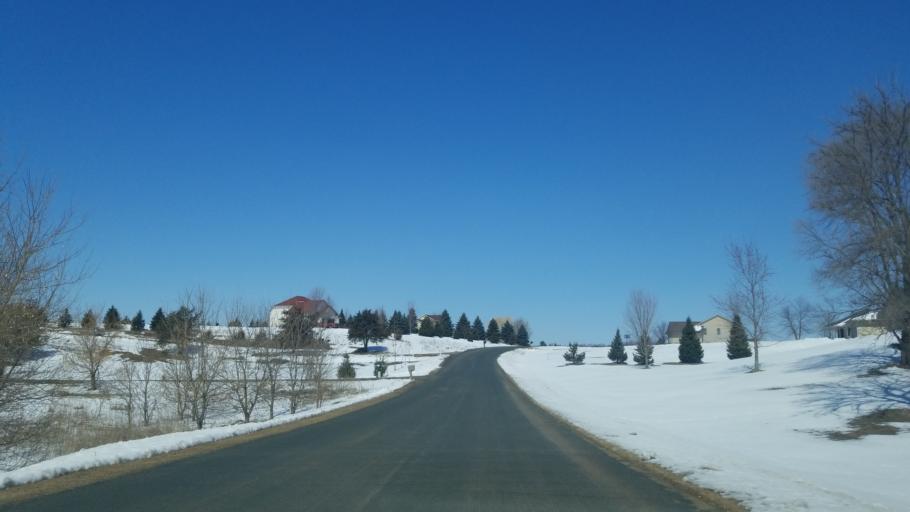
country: US
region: Wisconsin
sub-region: Saint Croix County
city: North Hudson
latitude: 44.9939
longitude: -92.6582
